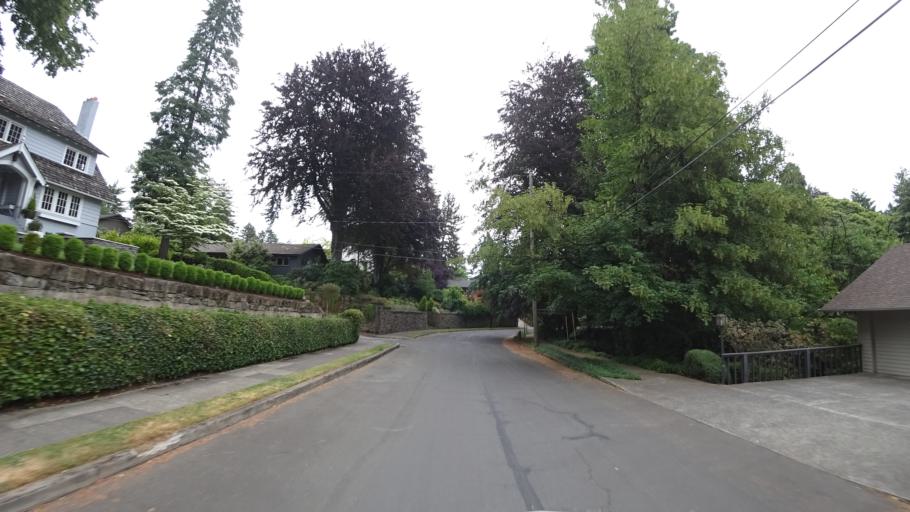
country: US
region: Oregon
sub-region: Multnomah County
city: Lents
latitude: 45.5180
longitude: -122.5952
